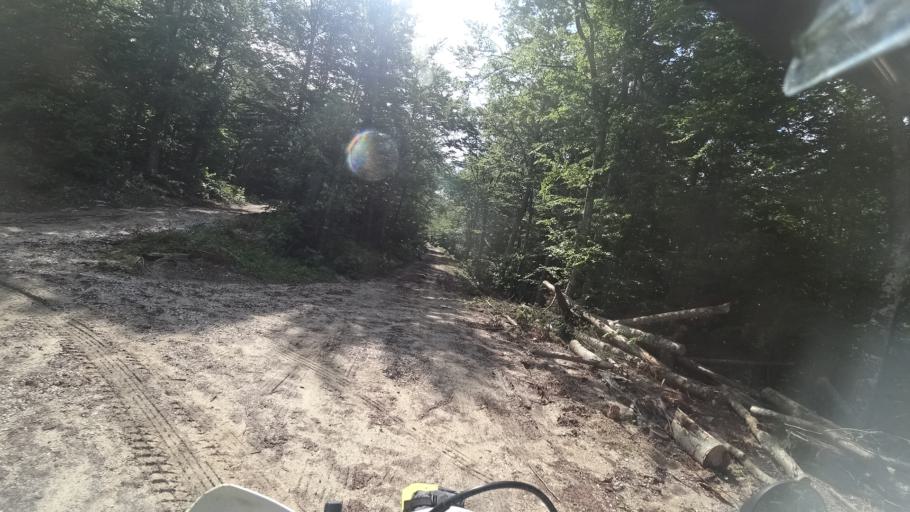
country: BA
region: Federation of Bosnia and Herzegovina
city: Izacic
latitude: 44.7878
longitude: 15.7287
